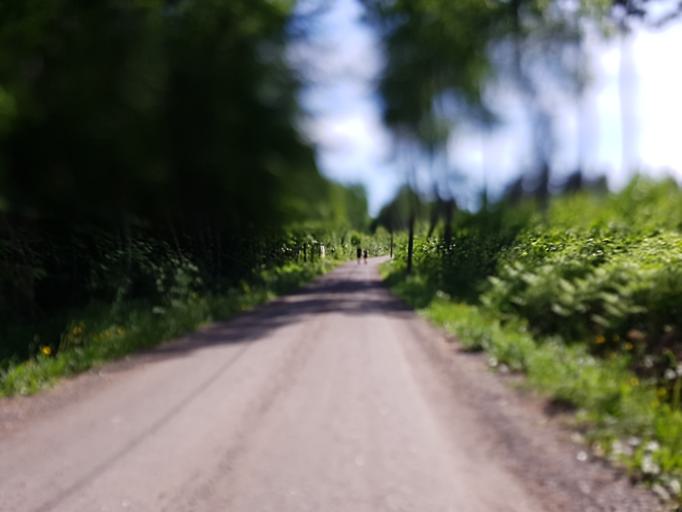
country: FI
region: Uusimaa
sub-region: Helsinki
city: Helsinki
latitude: 60.2918
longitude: 24.9166
